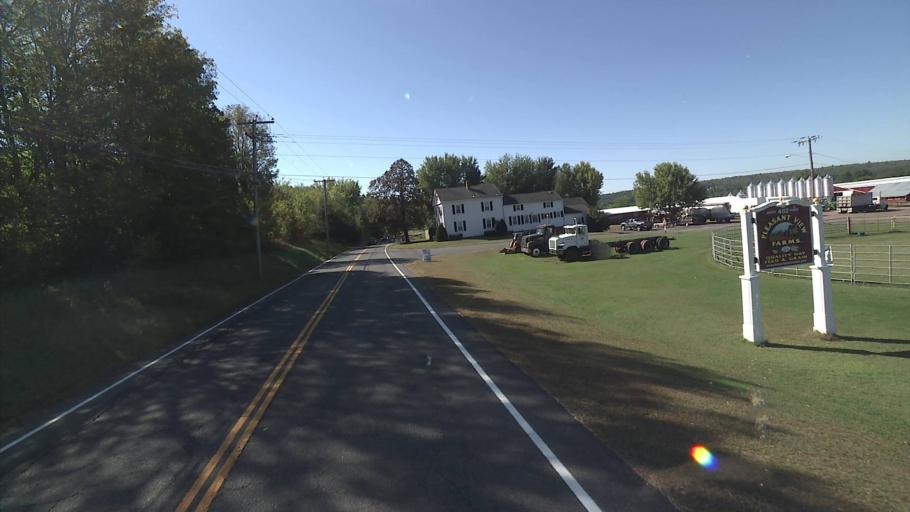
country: US
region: Connecticut
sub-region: Tolland County
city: Somers
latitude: 41.9567
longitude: -72.4448
